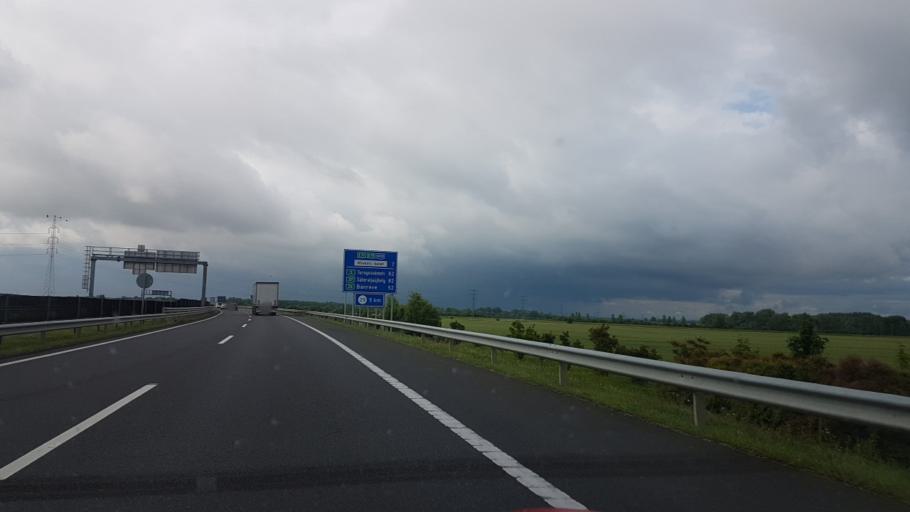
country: HU
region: Borsod-Abauj-Zemplen
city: Alsozsolca
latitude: 48.0685
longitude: 20.8482
